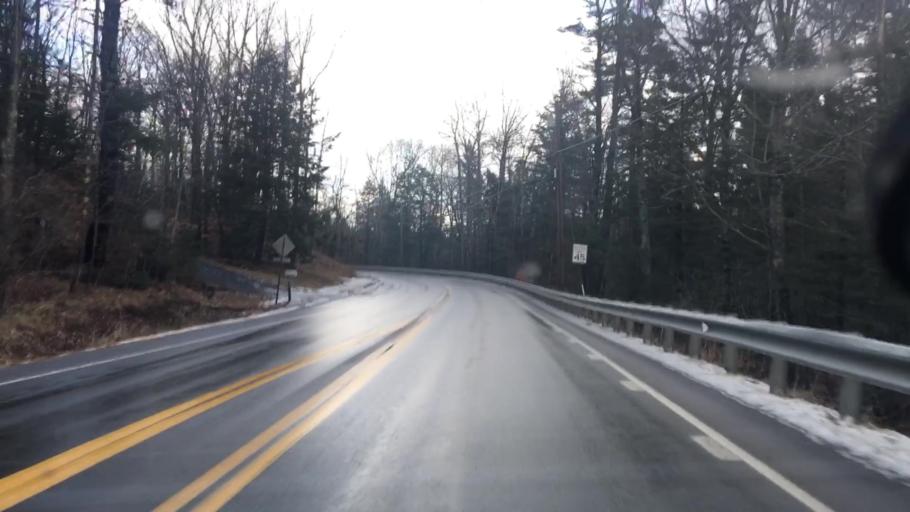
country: US
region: Maine
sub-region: Hancock County
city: Orland
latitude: 44.6309
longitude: -68.7023
